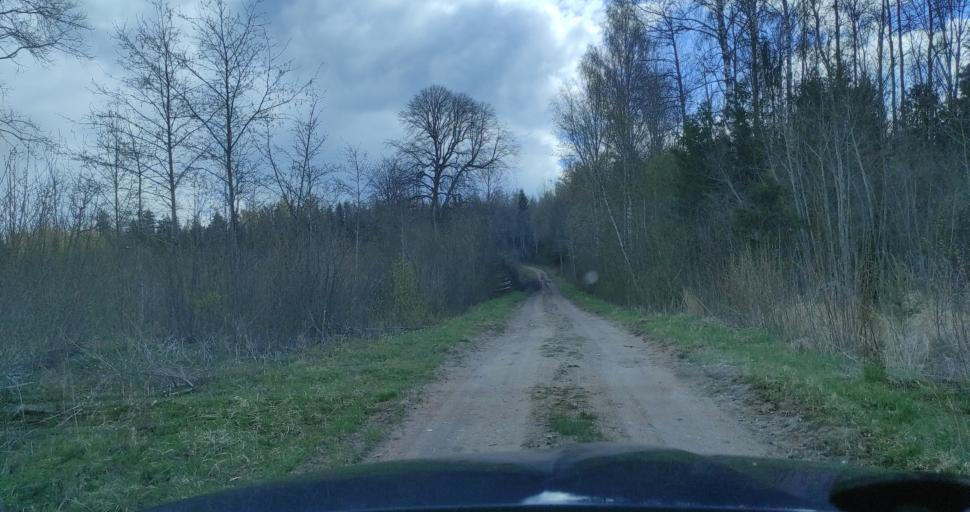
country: LV
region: Kuldigas Rajons
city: Kuldiga
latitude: 56.8650
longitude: 21.8286
